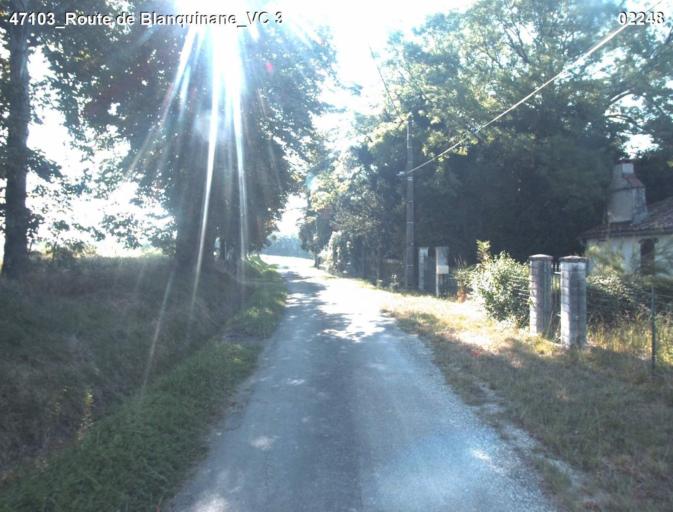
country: FR
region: Aquitaine
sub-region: Departement du Lot-et-Garonne
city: Nerac
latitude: 44.0868
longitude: 0.3387
